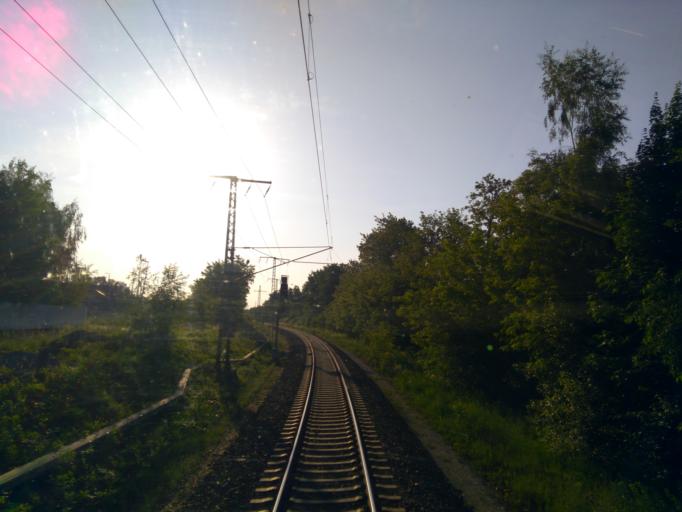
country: DE
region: Brandenburg
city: Cottbus
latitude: 51.7491
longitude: 14.2996
